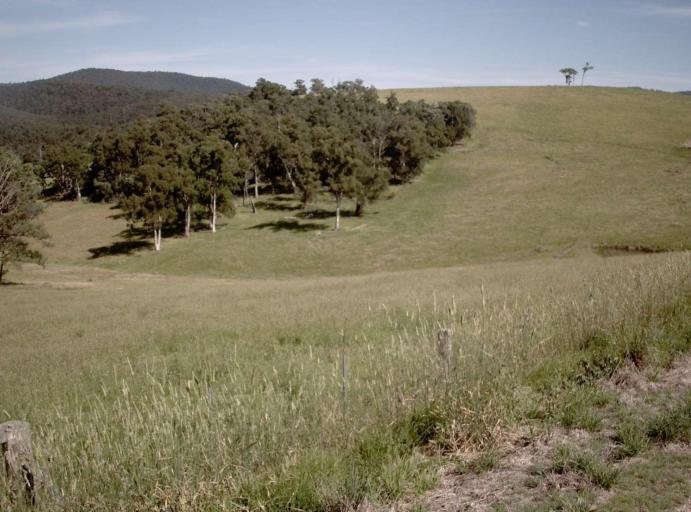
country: AU
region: Victoria
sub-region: East Gippsland
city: Lakes Entrance
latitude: -37.4983
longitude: 148.1324
